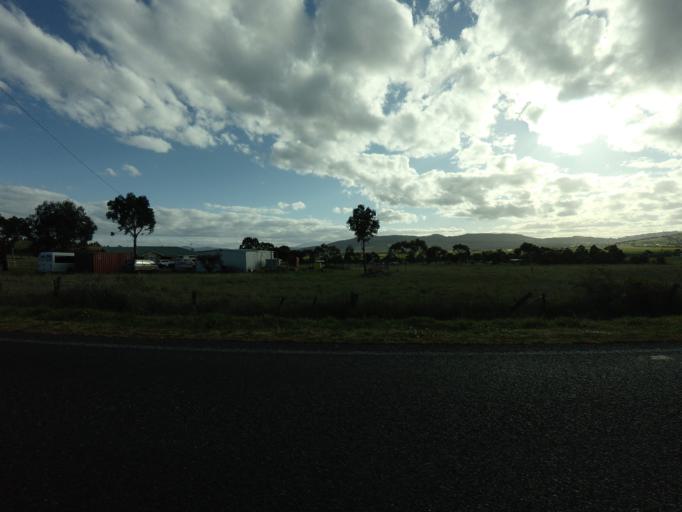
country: AU
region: Tasmania
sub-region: Sorell
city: Sorell
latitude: -42.7666
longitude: 147.5453
